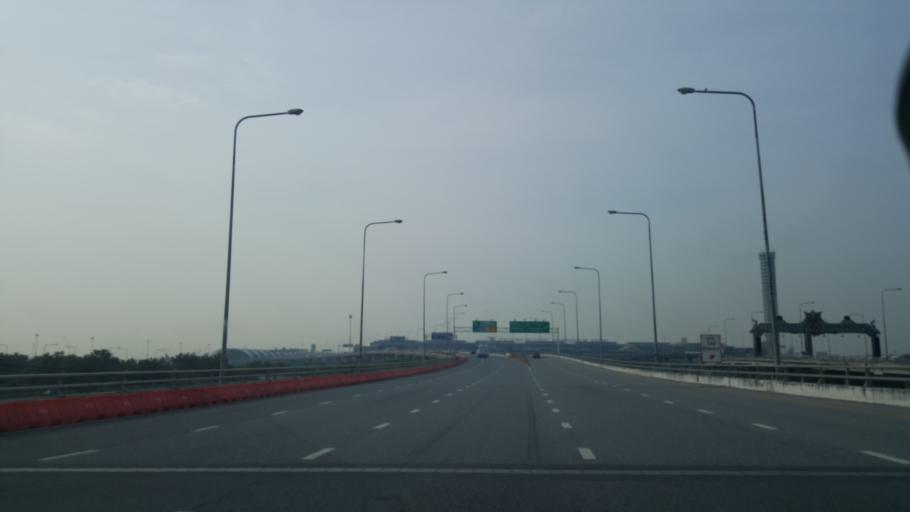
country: TH
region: Bangkok
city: Lat Krabang
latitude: 13.7029
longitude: 100.7540
